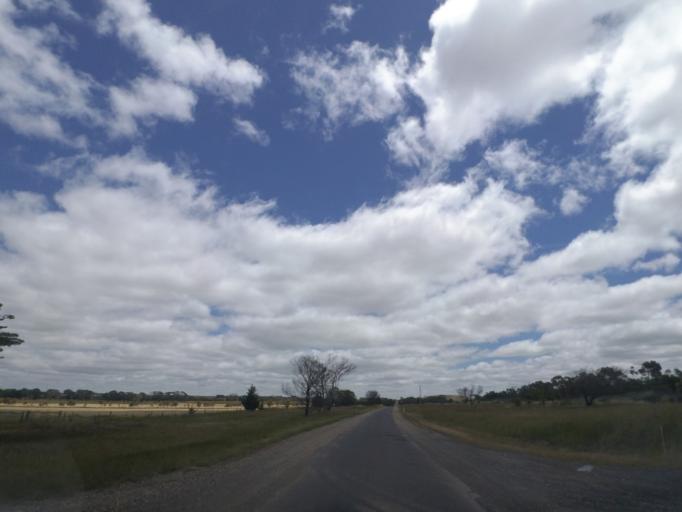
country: AU
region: Victoria
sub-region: Moorabool
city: Bacchus Marsh
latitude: -37.6341
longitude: 144.2715
